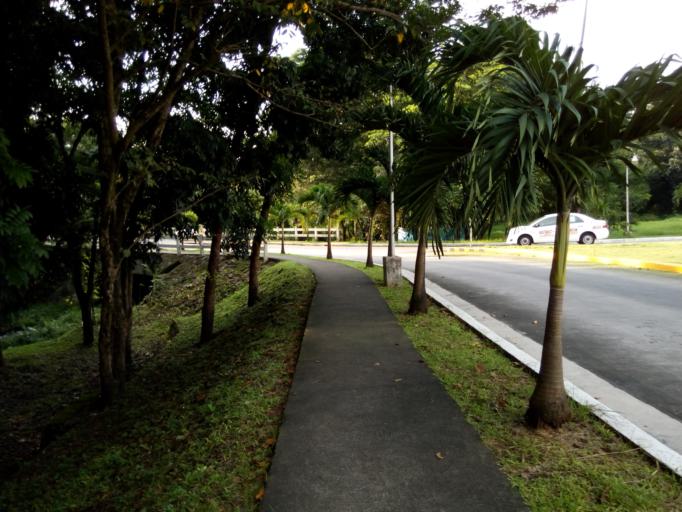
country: PH
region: Metro Manila
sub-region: Quezon City
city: Quezon City
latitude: 14.6496
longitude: 121.0704
